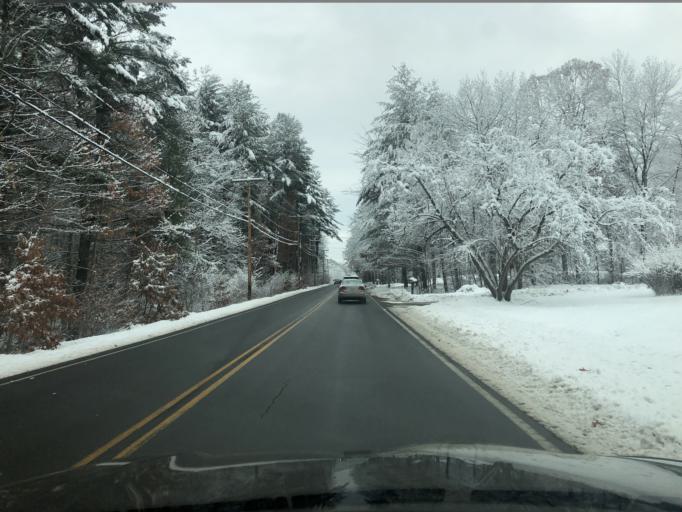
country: US
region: New Hampshire
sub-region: Strafford County
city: Somersworth
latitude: 43.2295
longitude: -70.8632
